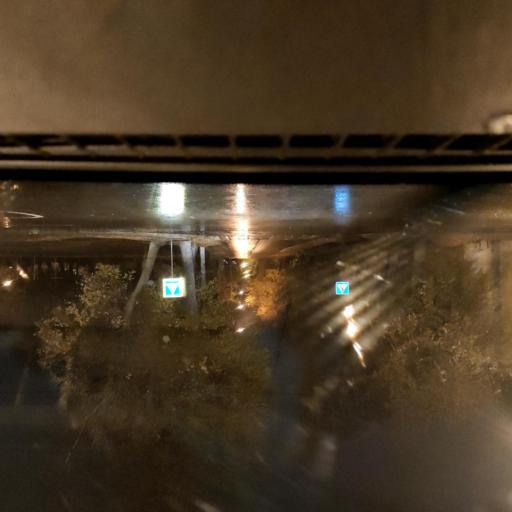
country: RU
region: Voronezj
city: Maslovka
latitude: 51.6166
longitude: 39.2484
